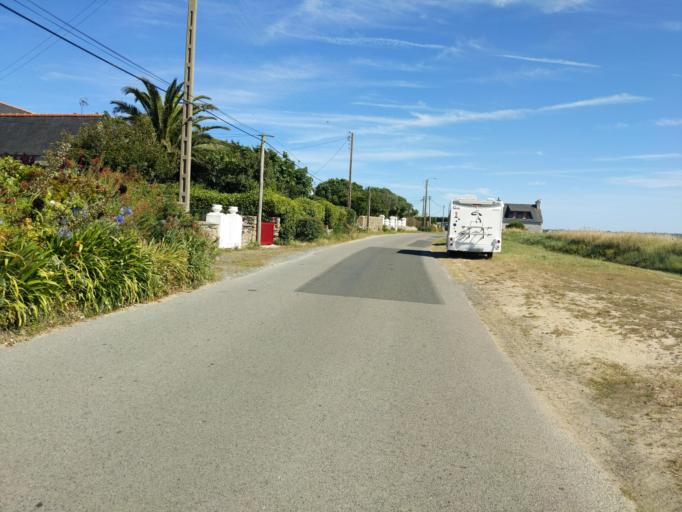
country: FR
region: Brittany
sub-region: Departement des Cotes-d'Armor
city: Pleubian
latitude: 48.8616
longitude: -3.0827
